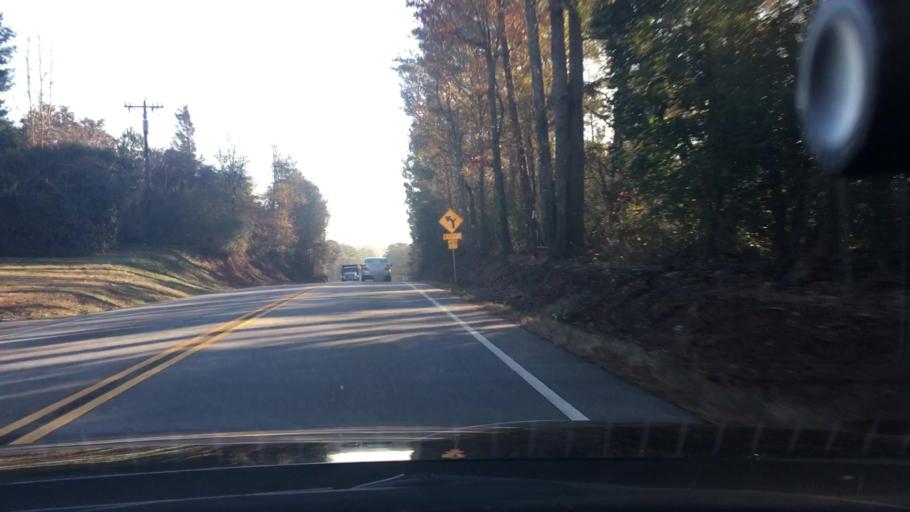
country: US
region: Georgia
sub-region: Spalding County
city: Experiment
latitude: 33.2390
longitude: -84.3252
